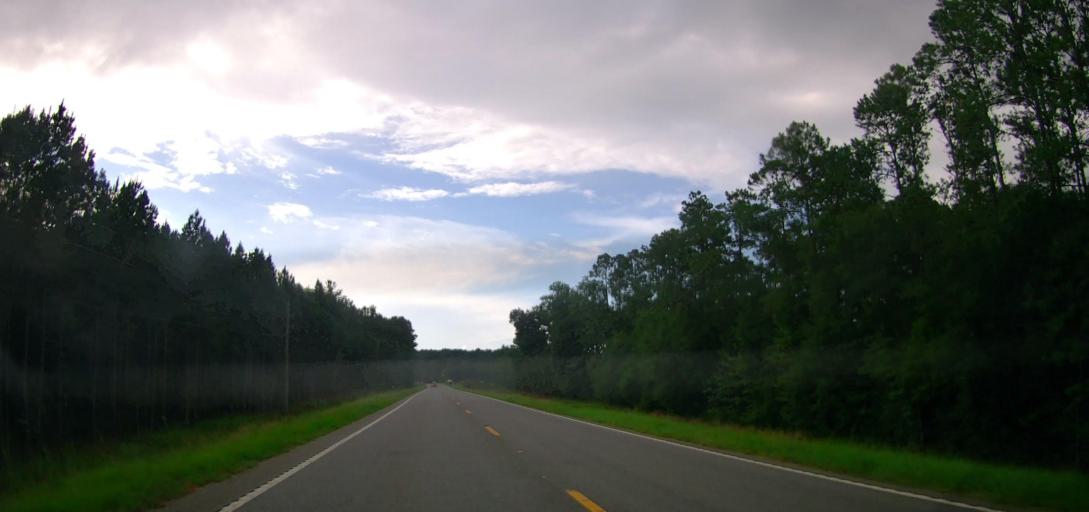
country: US
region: Georgia
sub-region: Ware County
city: Deenwood
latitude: 31.3065
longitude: -82.5637
